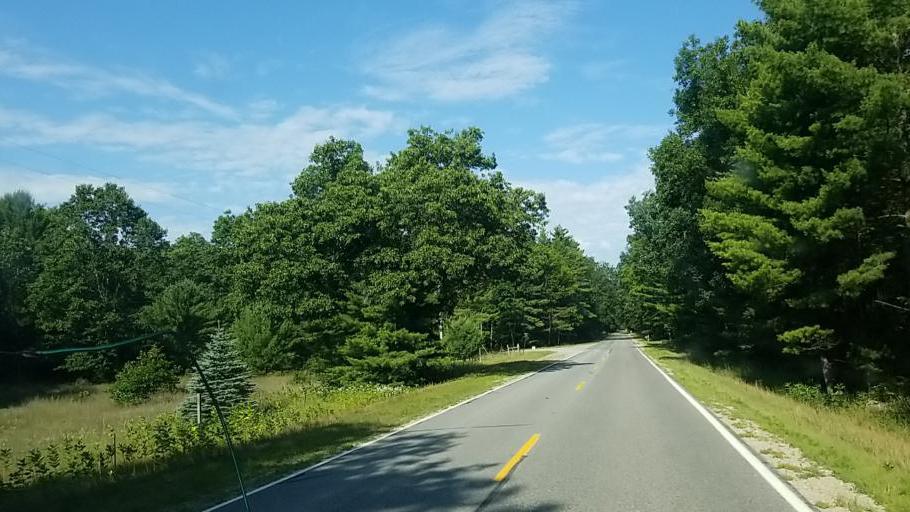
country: US
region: Michigan
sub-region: Muskegon County
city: Twin Lake
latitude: 43.4688
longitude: -86.1770
